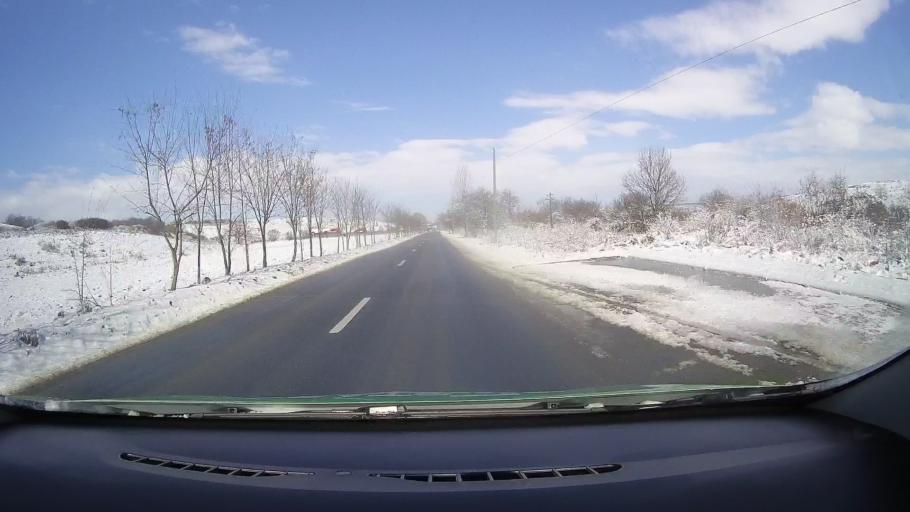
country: RO
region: Sibiu
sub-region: Comuna Nocrich
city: Nocrich
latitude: 45.8743
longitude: 24.4513
